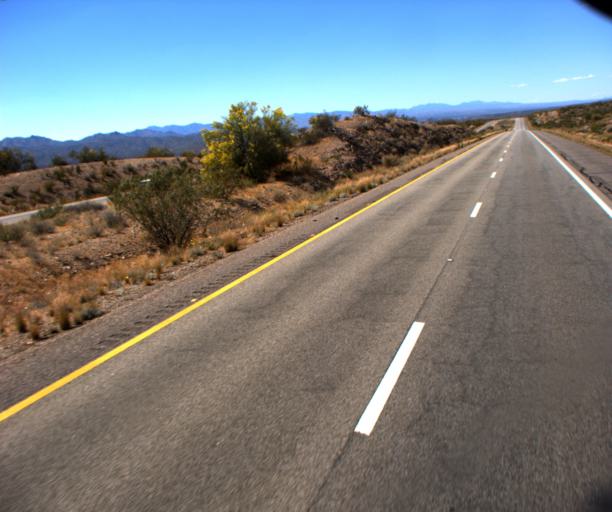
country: US
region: Arizona
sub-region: Yavapai County
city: Bagdad
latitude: 34.6016
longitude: -113.5195
